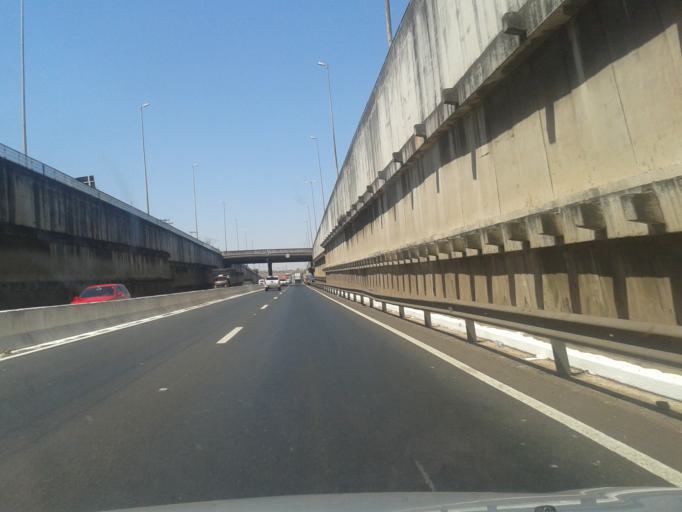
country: BR
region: Minas Gerais
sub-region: Uberlandia
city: Uberlandia
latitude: -18.8985
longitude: -48.2431
